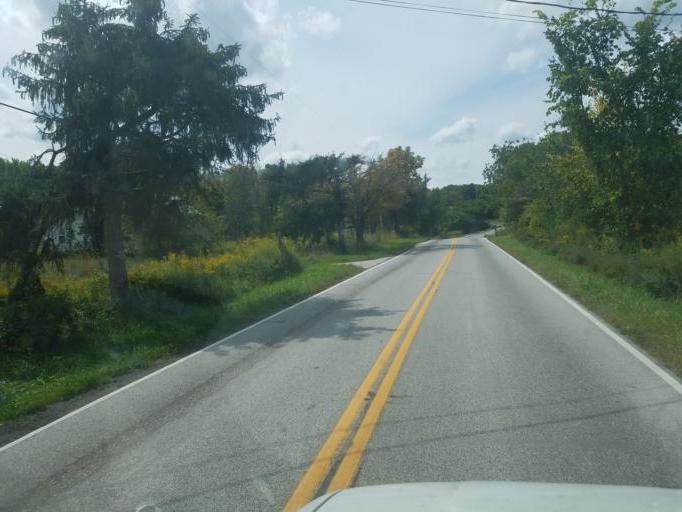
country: US
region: Ohio
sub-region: Geauga County
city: Middlefield
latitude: 41.4128
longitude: -81.0194
